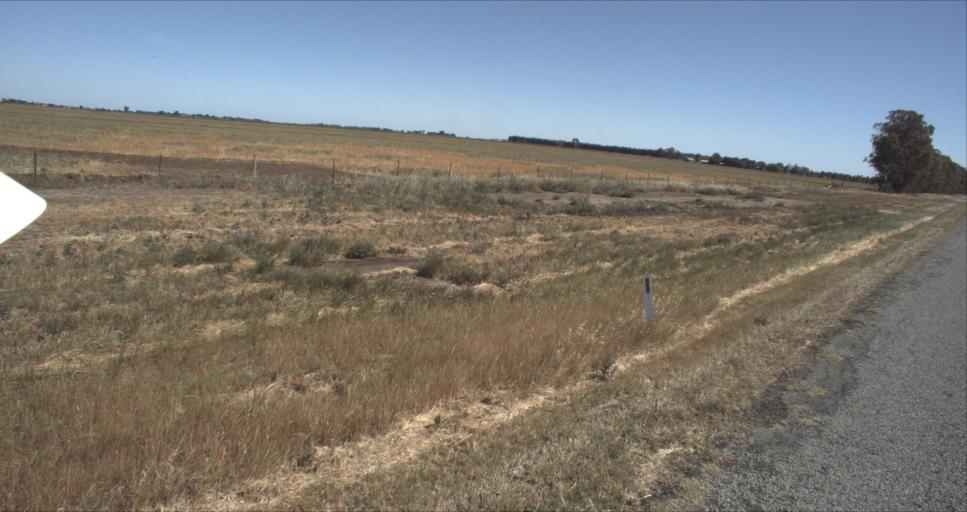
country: AU
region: New South Wales
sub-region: Leeton
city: Leeton
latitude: -34.5383
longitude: 146.3170
